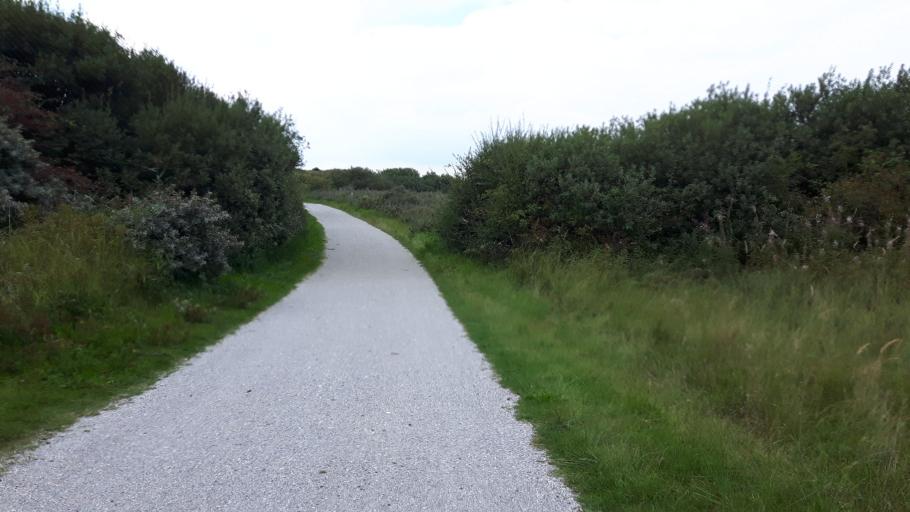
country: NL
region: Friesland
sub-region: Gemeente Dongeradeel
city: Holwerd
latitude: 53.4625
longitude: 5.9003
